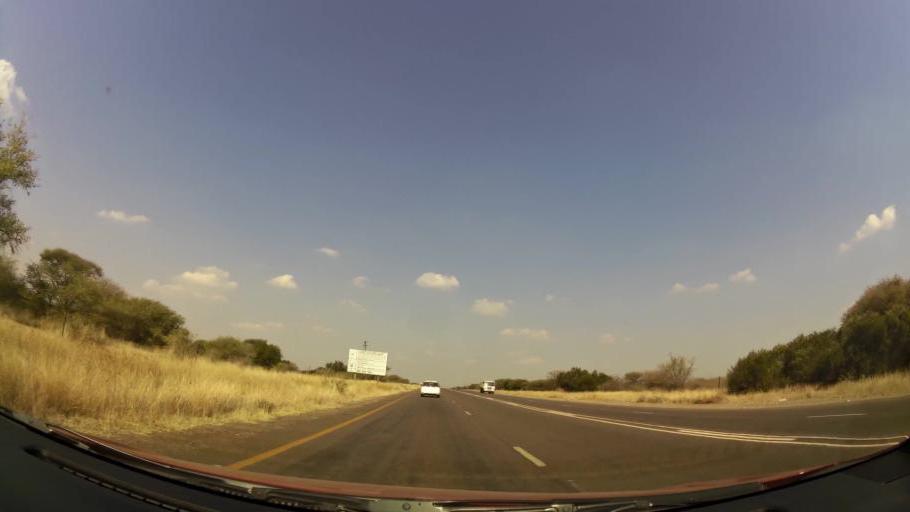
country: ZA
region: North-West
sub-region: Bojanala Platinum District Municipality
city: Mogwase
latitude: -25.3958
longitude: 27.0717
